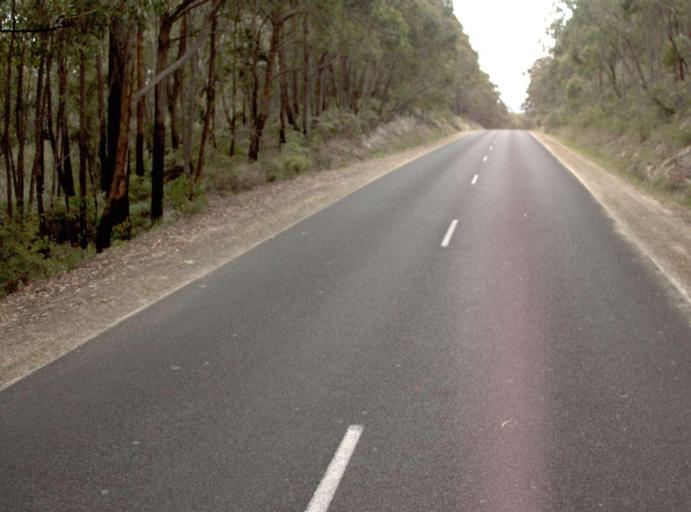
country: AU
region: Victoria
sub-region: Latrobe
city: Traralgon
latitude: -38.3975
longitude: 146.8161
